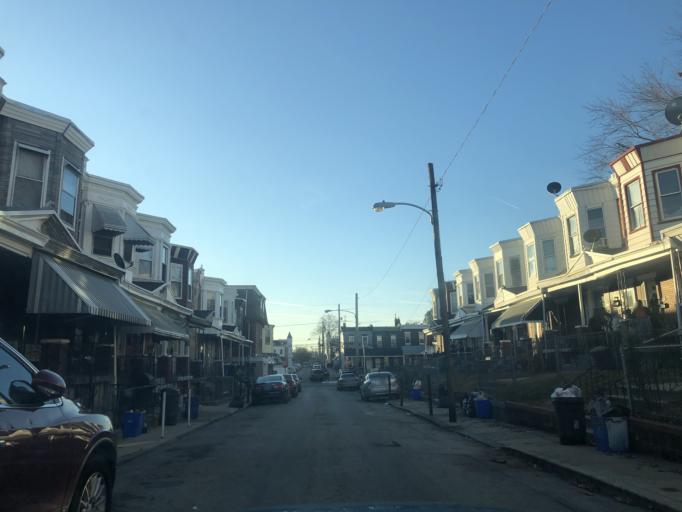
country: US
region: Pennsylvania
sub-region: Delaware County
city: Millbourne
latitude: 39.9744
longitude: -75.2323
